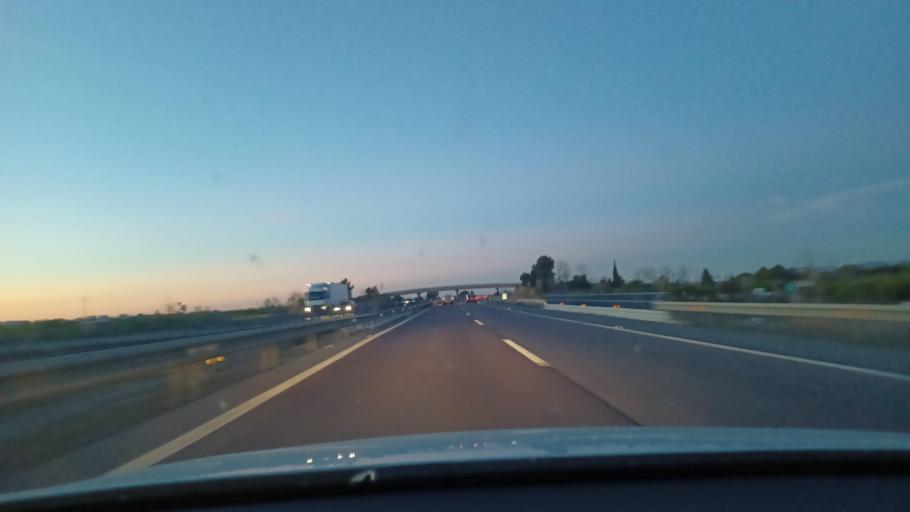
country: ES
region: Valencia
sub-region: Provincia de Castello
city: Nules
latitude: 39.8493
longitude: -0.1251
